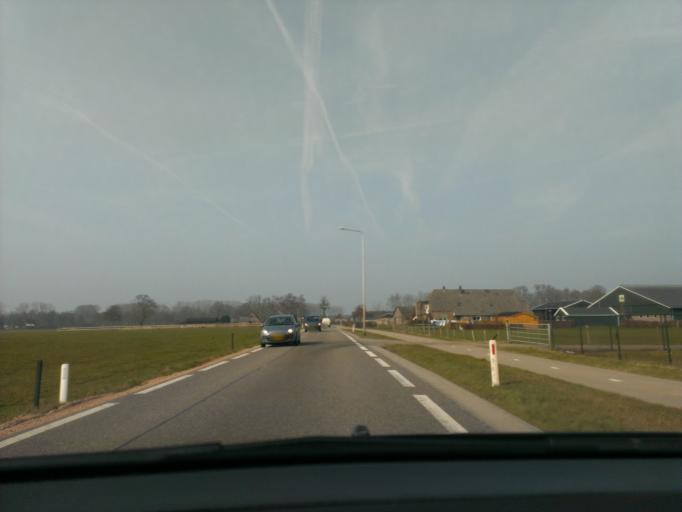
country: NL
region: Gelderland
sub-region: Gemeente Epe
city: Emst
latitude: 52.2918
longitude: 6.0225
